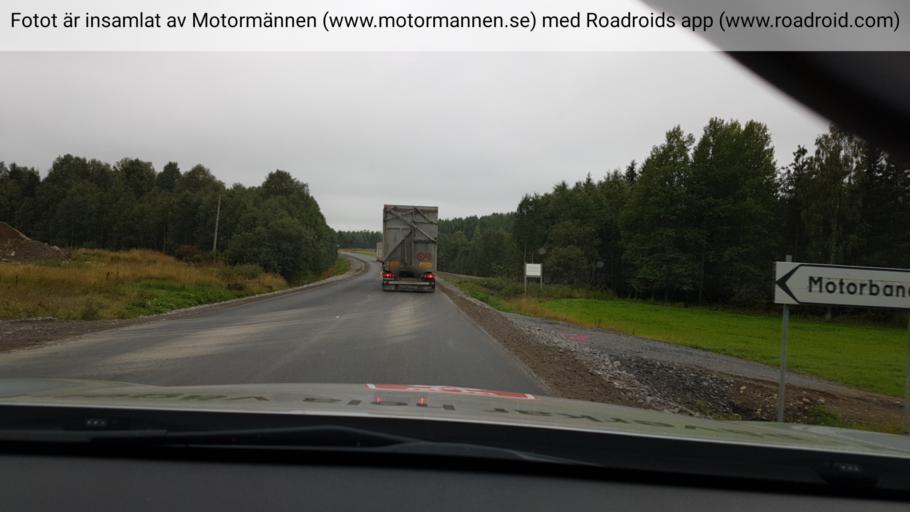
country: SE
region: Vaesterbotten
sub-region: Skelleftea Kommun
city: Burtraesk
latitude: 64.3683
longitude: 20.5025
